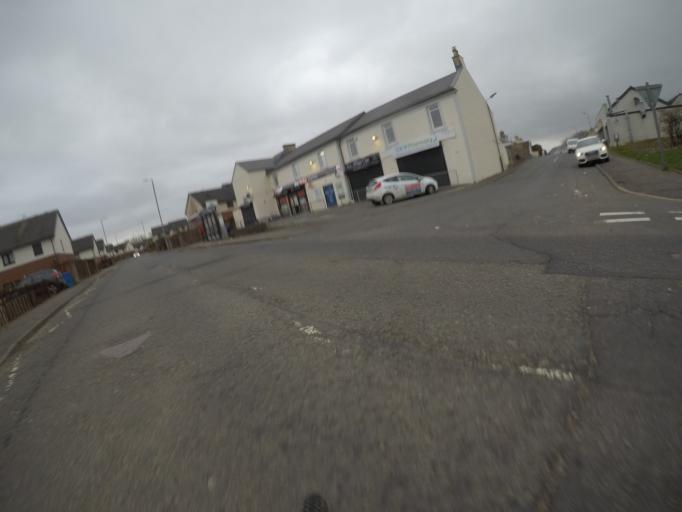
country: GB
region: Scotland
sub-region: North Ayrshire
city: Springside
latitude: 55.6139
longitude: -4.5883
